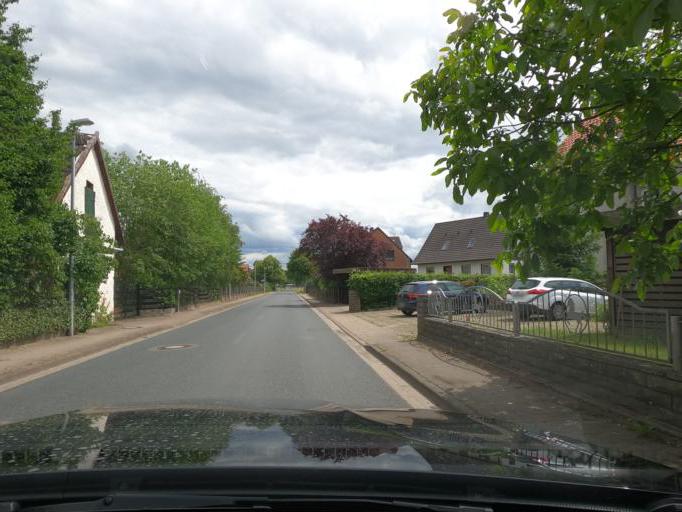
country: DE
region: Lower Saxony
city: Lehrte
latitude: 52.4207
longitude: 9.9547
